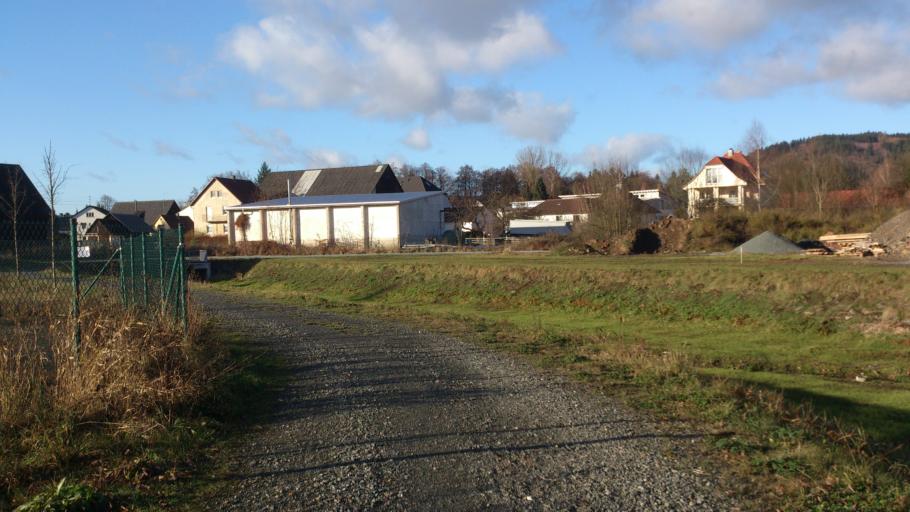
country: DE
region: Bavaria
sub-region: Upper Franconia
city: Stadtsteinach
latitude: 50.1631
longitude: 11.5086
